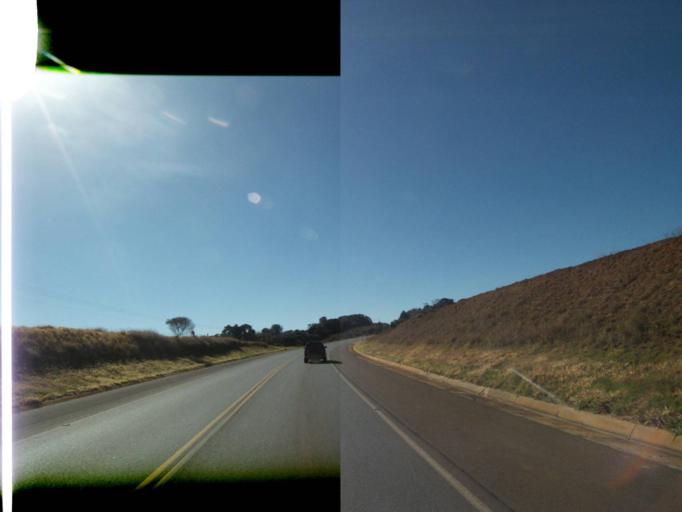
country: BR
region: Parana
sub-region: Tibagi
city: Tibagi
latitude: -24.3702
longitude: -50.3263
